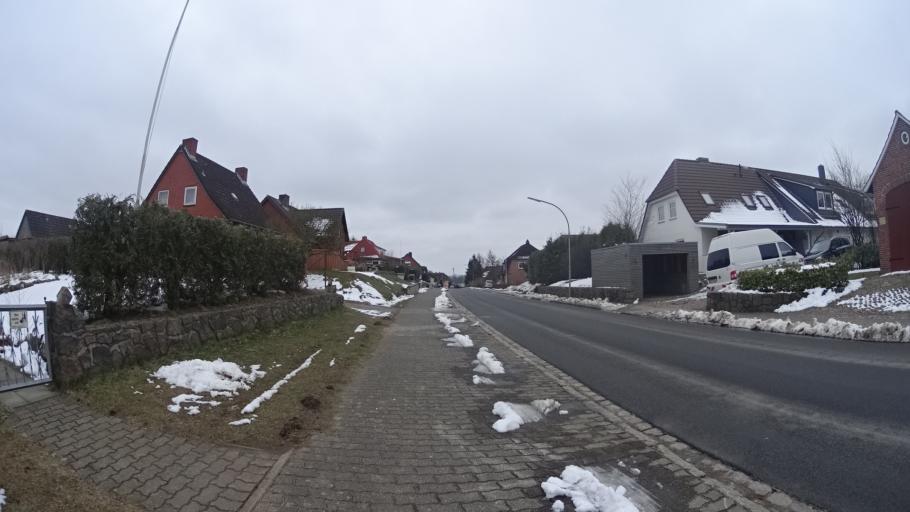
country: DE
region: Schleswig-Holstein
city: Panker
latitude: 54.3124
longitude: 10.5717
